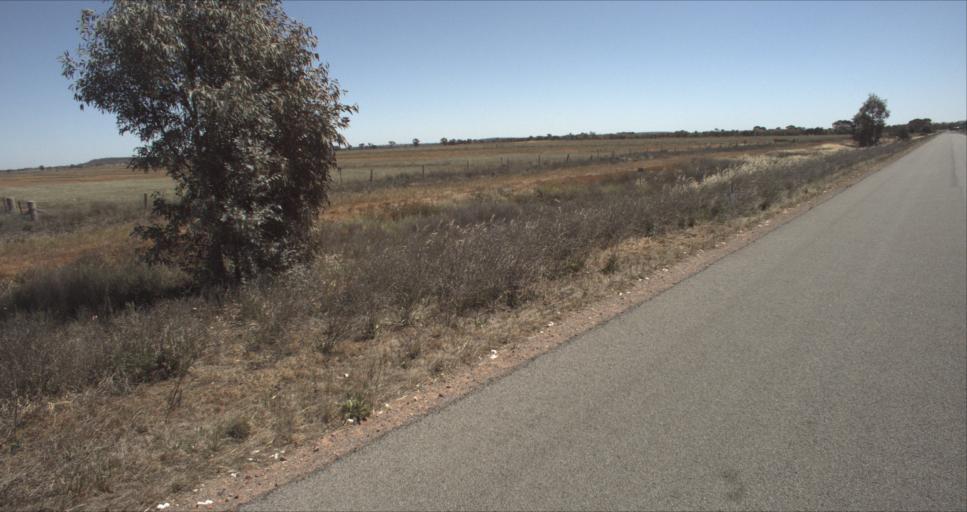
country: AU
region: New South Wales
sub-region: Leeton
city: Leeton
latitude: -34.4370
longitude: 146.2985
